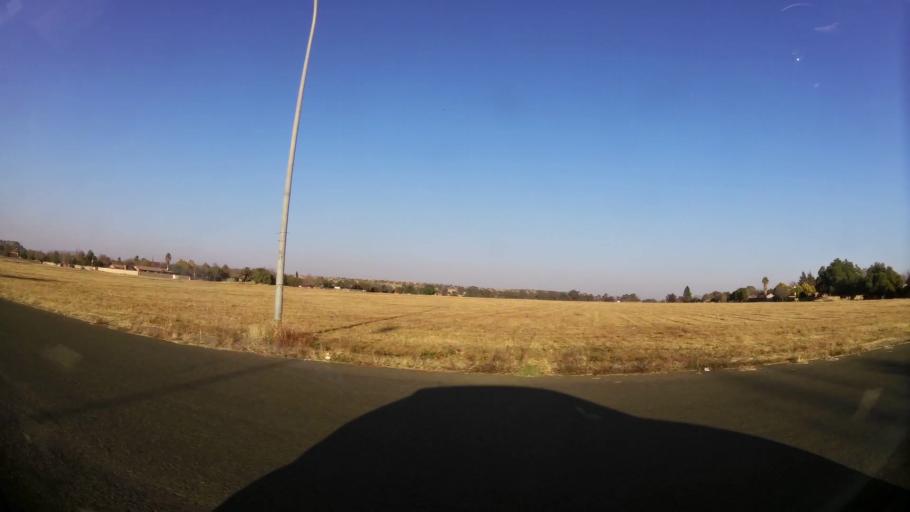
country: ZA
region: Orange Free State
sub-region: Mangaung Metropolitan Municipality
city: Bloemfontein
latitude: -29.1580
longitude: 26.1699
